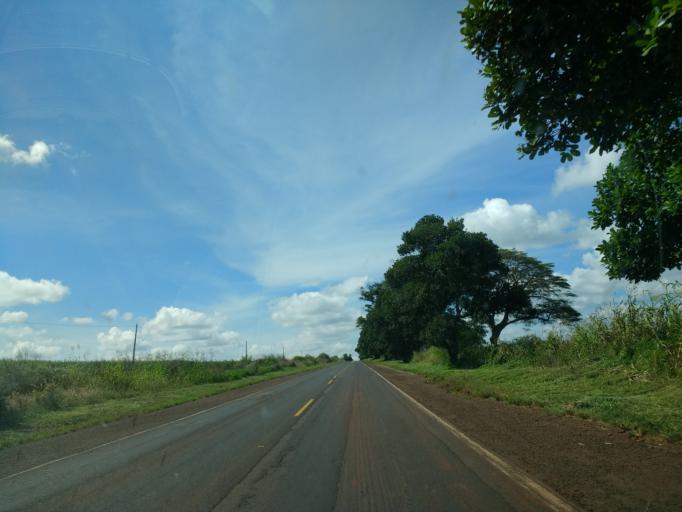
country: BR
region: Parana
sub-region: Paicandu
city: Paicandu
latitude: -23.4854
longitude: -52.0853
